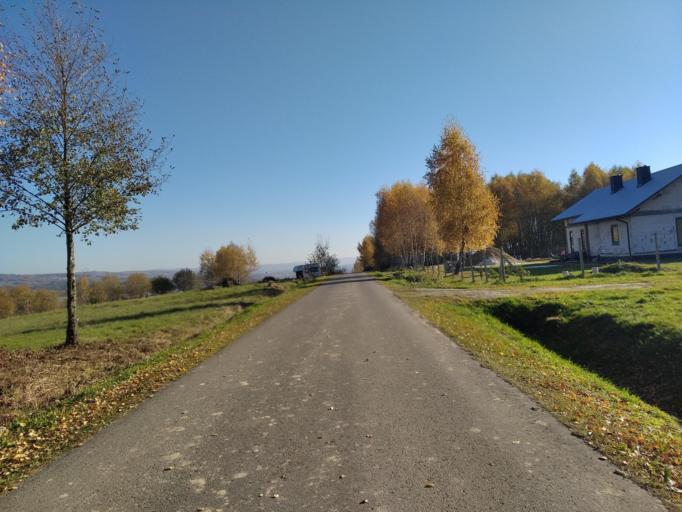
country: PL
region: Subcarpathian Voivodeship
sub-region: Powiat strzyzowski
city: Frysztak
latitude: 49.8615
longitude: 21.6130
